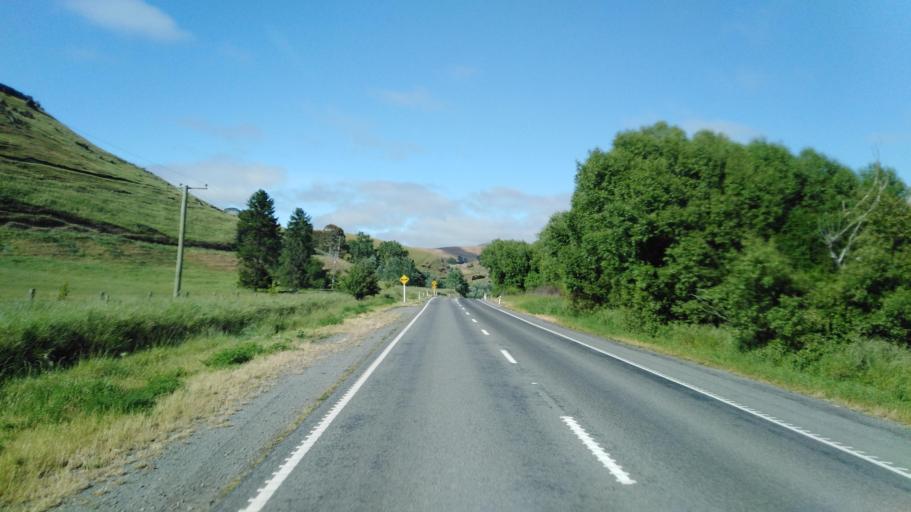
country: NZ
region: Canterbury
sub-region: Hurunui District
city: Amberley
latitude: -43.0030
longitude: 172.7103
